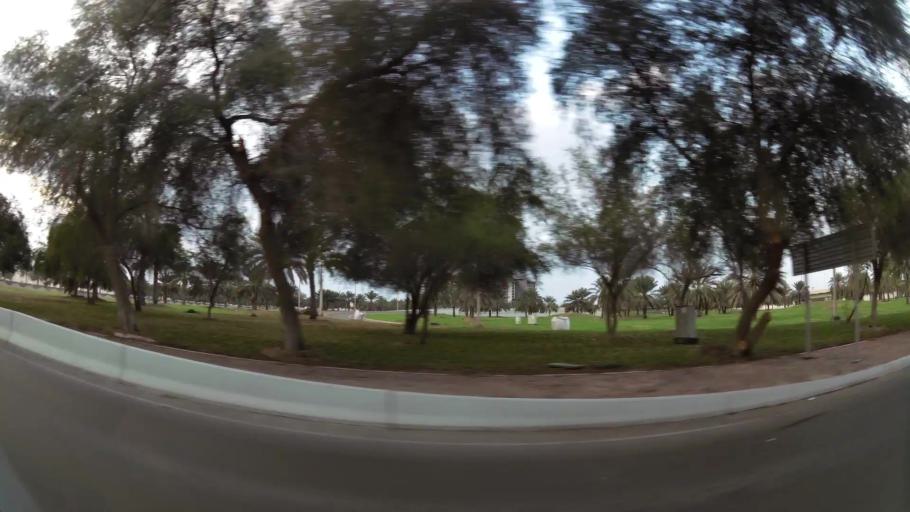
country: AE
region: Abu Dhabi
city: Abu Dhabi
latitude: 24.4187
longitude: 54.4757
